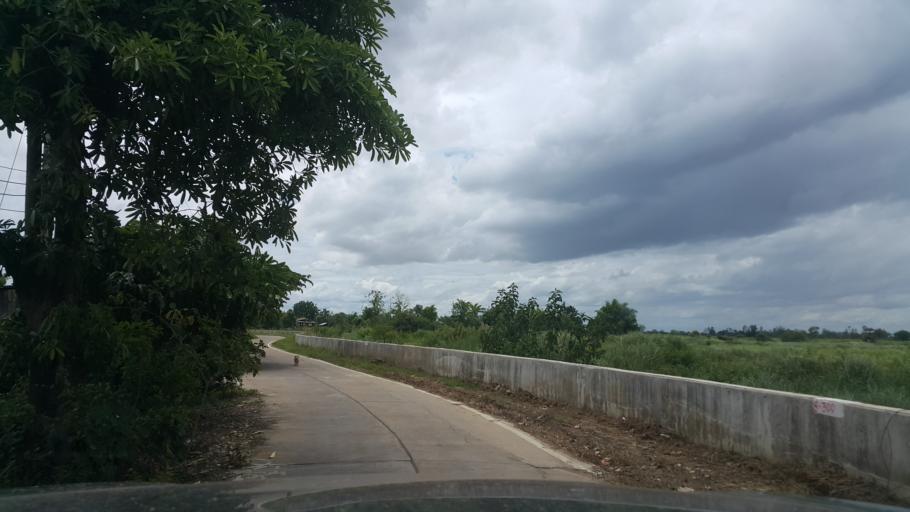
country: TH
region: Sukhothai
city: Sukhothai
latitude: 17.0179
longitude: 99.8072
